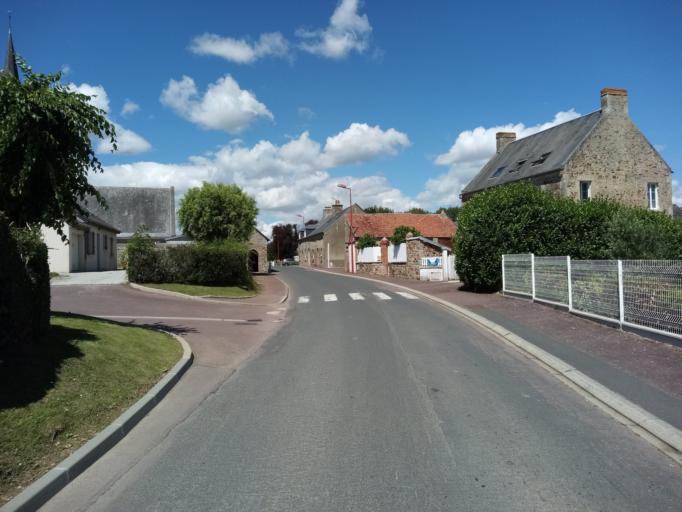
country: FR
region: Lower Normandy
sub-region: Departement de la Manche
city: Periers
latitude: 49.2805
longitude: -1.4241
